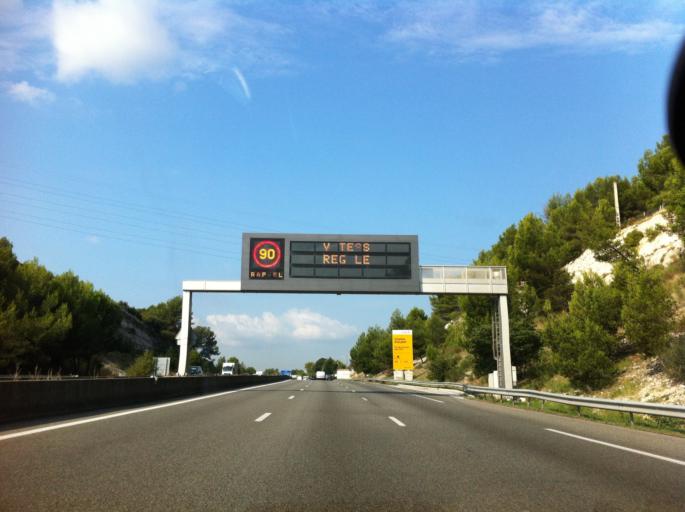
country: FR
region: Provence-Alpes-Cote d'Azur
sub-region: Departement des Bouches-du-Rhone
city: Meyreuil
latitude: 43.5132
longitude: 5.4774
